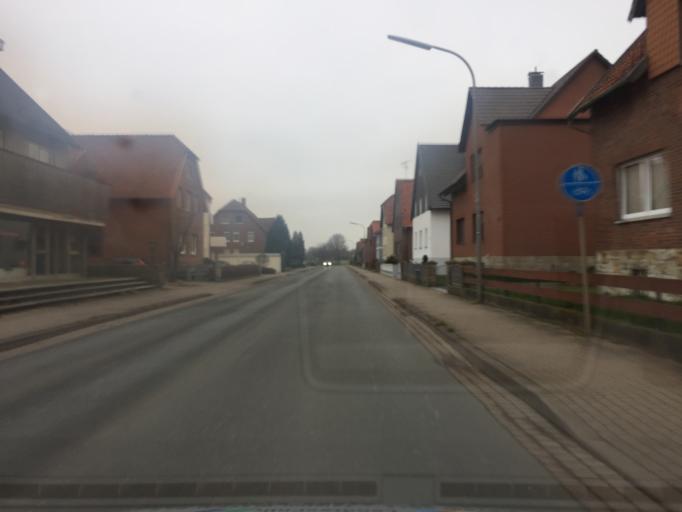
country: DE
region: Lower Saxony
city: Meerbeck
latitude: 52.3239
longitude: 9.1712
